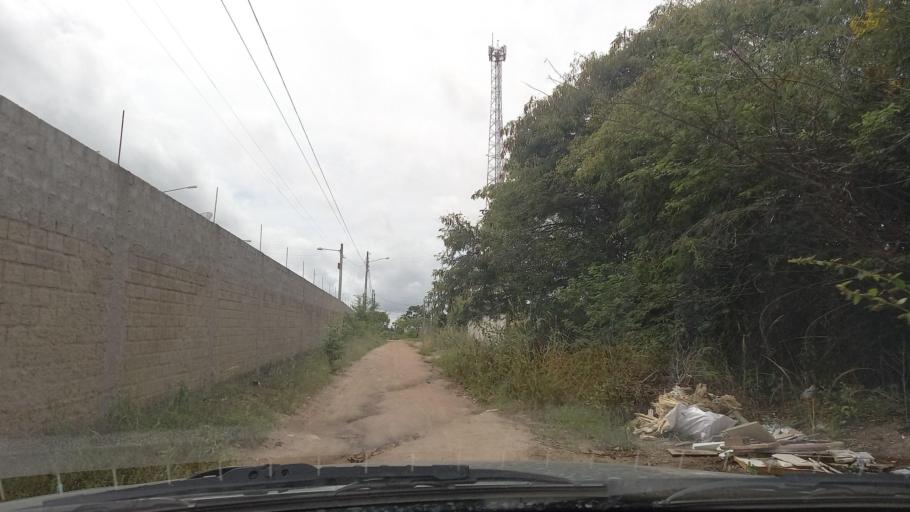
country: BR
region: Pernambuco
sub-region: Gravata
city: Gravata
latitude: -8.1927
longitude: -35.5924
